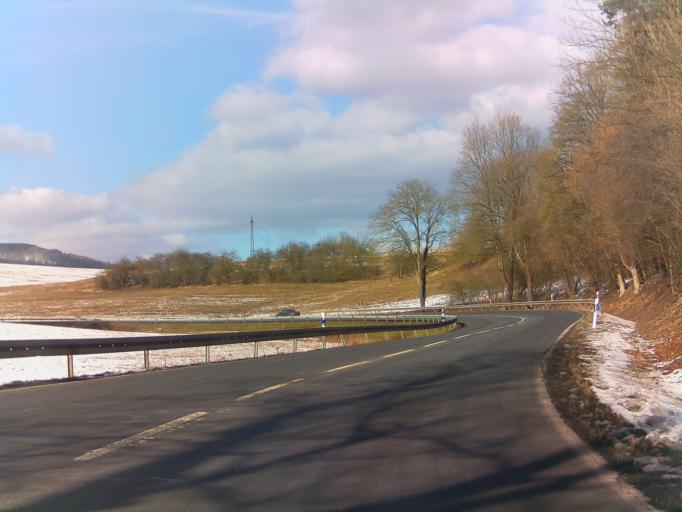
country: DE
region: Thuringia
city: Rohr
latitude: 50.6034
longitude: 10.5112
